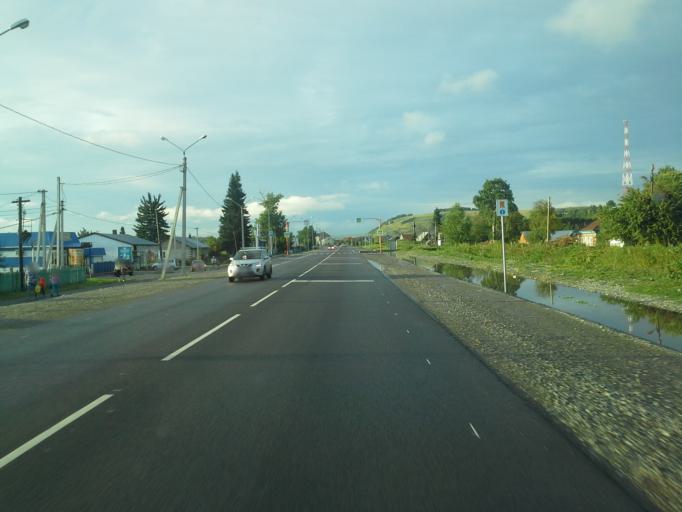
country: RU
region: Khabarovsk Krai
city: Mayma
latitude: 52.0207
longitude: 85.9176
